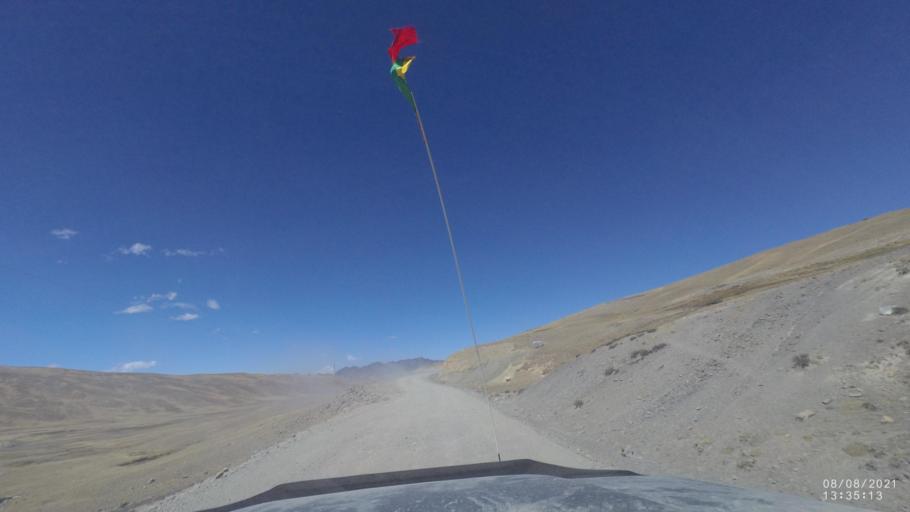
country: BO
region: Cochabamba
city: Colchani
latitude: -17.0668
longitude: -66.5092
